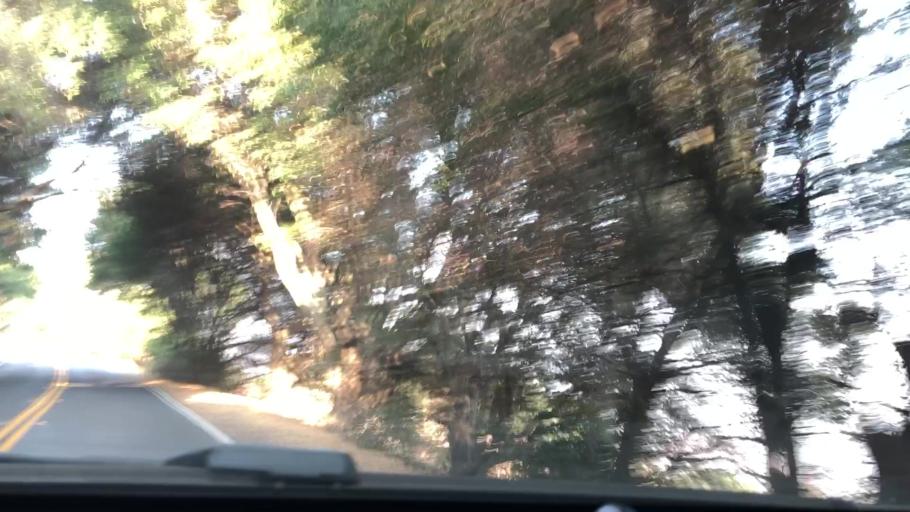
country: US
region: California
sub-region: Alameda County
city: Berkeley
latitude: 37.8987
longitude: -122.2308
